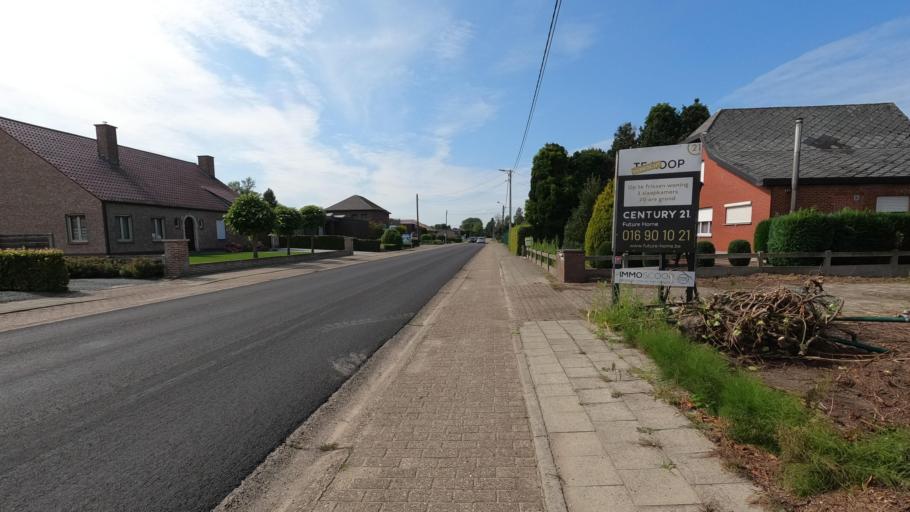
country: BE
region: Flanders
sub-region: Provincie Vlaams-Brabant
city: Begijnendijk
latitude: 51.0340
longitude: 4.7434
